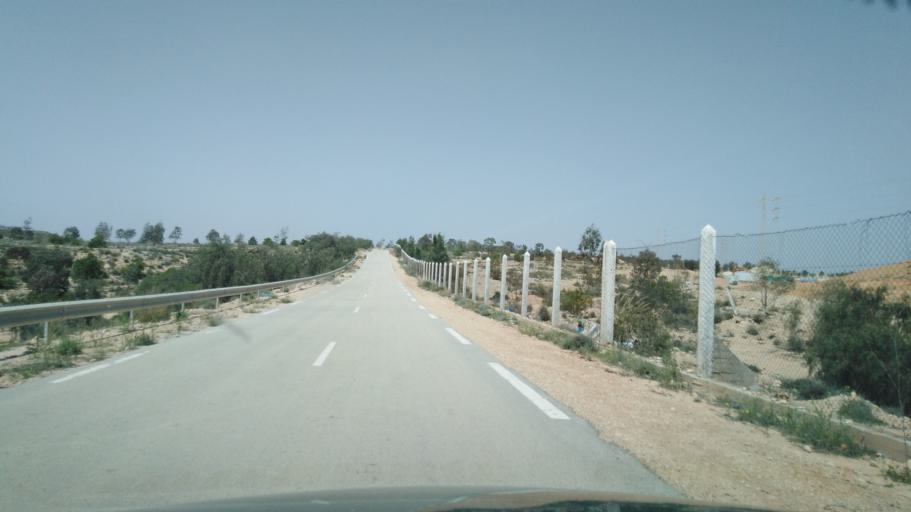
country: TN
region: Safaqis
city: Sfax
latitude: 34.7066
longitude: 10.5255
